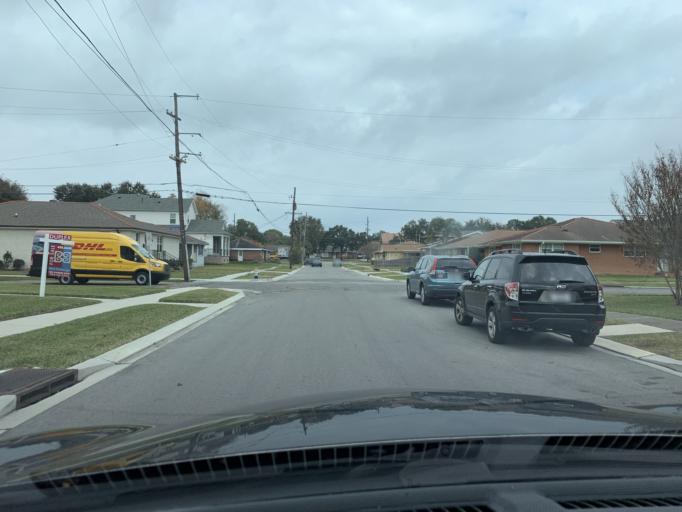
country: US
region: Louisiana
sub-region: Jefferson Parish
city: Metairie
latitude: 30.0178
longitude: -90.1022
